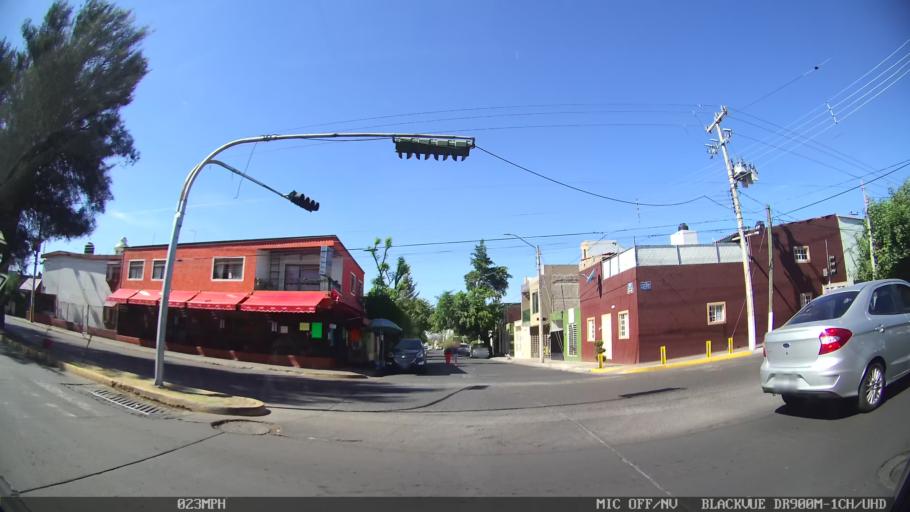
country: MX
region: Jalisco
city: Tlaquepaque
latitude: 20.6793
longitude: -103.2800
